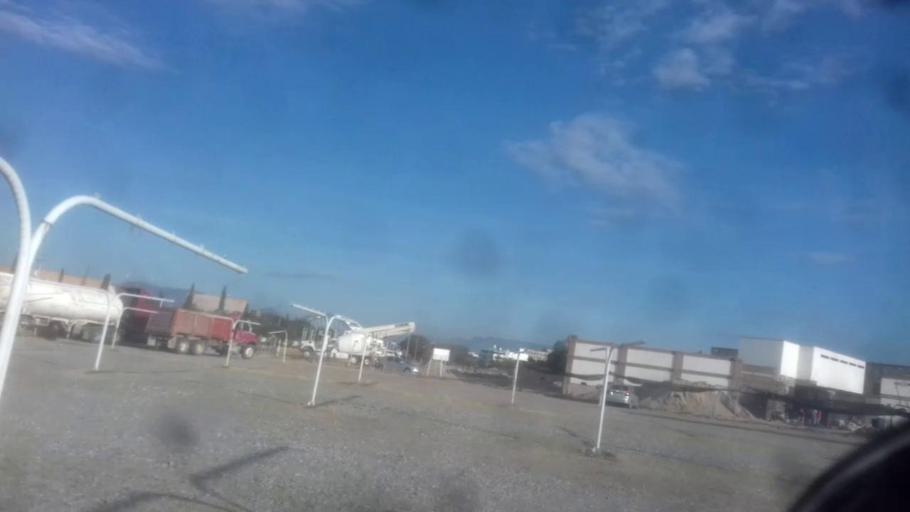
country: MX
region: Aguascalientes
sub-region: Aguascalientes
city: Aguascalientes
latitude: 21.8564
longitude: -102.2866
